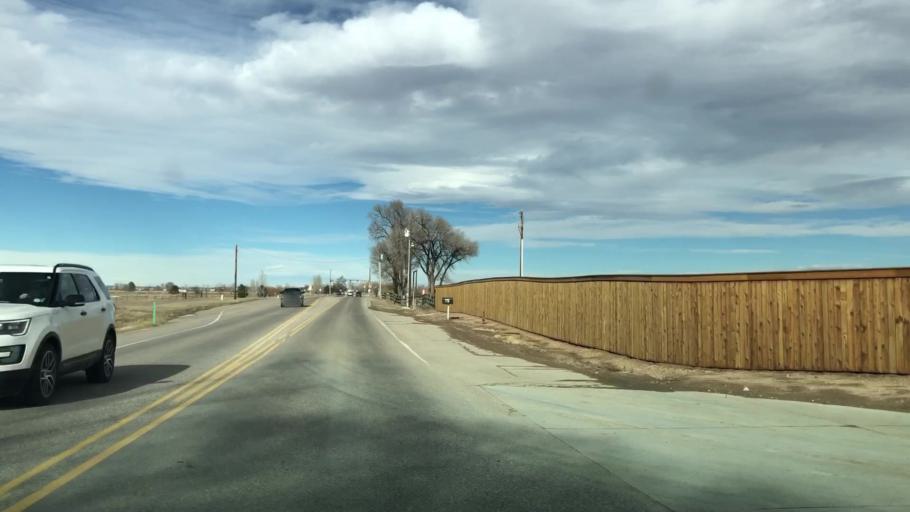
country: US
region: Colorado
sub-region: Weld County
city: Windsor
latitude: 40.4757
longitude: -104.9441
